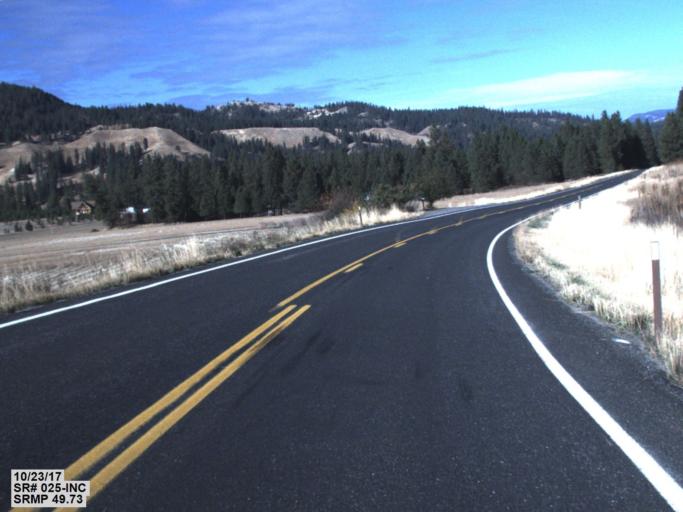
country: US
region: Washington
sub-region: Stevens County
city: Kettle Falls
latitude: 48.2048
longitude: -118.1800
